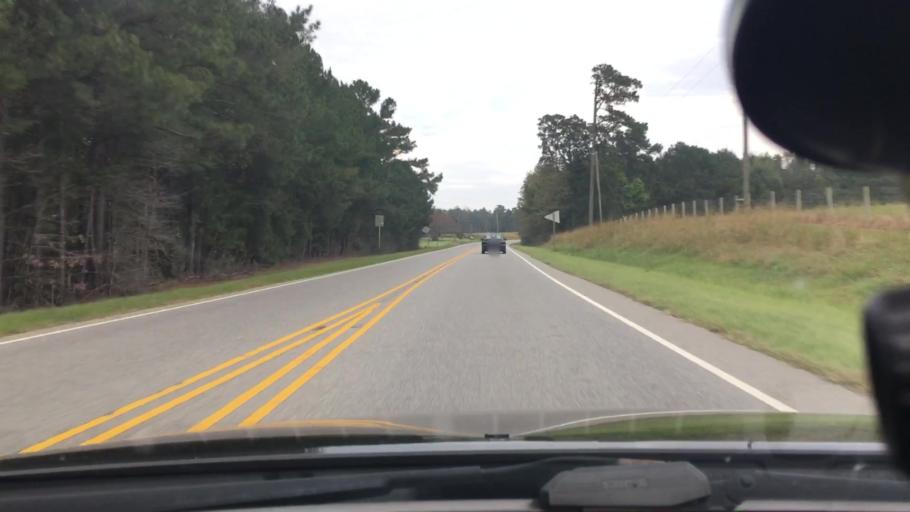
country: US
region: North Carolina
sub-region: Moore County
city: Robbins
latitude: 35.3767
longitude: -79.6669
